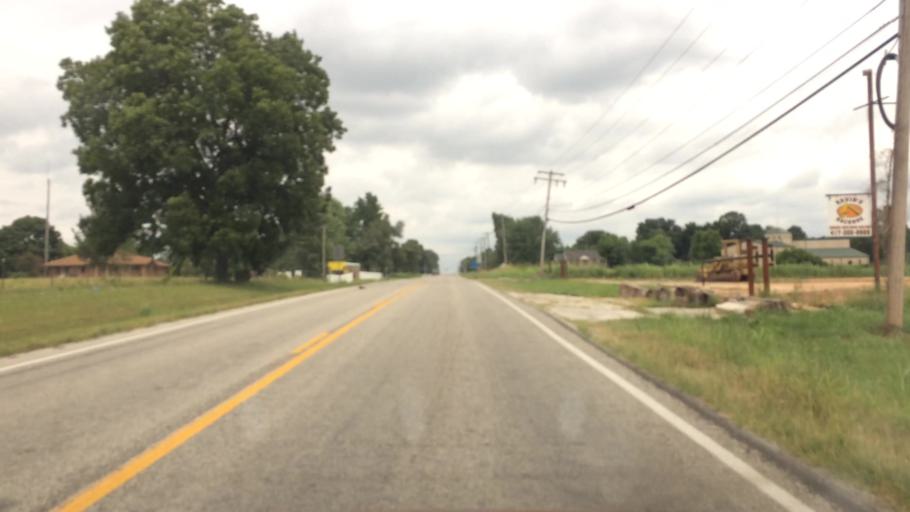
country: US
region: Missouri
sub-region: Greene County
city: Springfield
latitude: 37.2919
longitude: -93.2638
